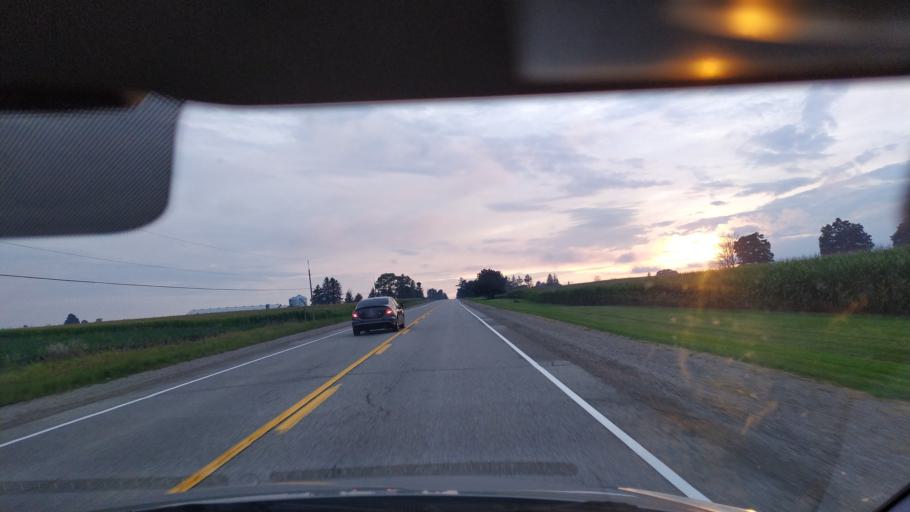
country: CA
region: Ontario
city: Kitchener
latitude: 43.3079
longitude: -80.5921
